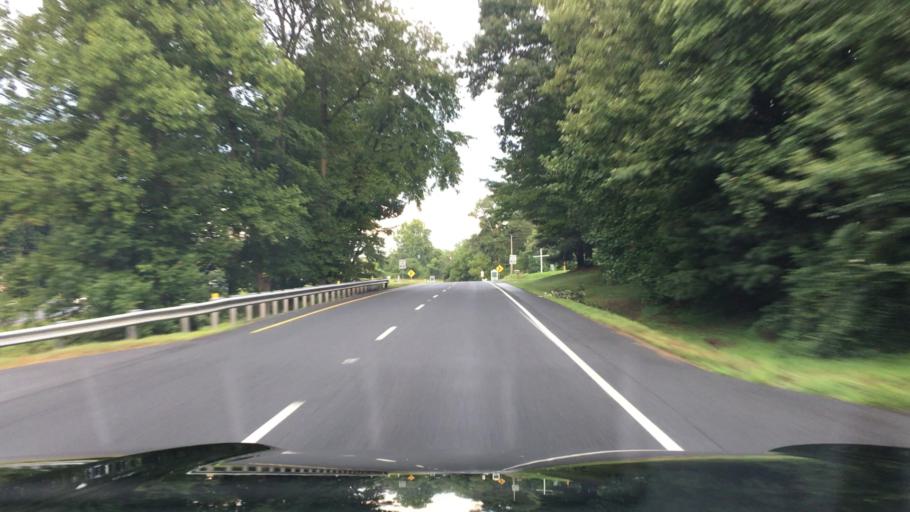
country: US
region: Virginia
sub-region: Culpeper County
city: Merrimac
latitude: 38.4497
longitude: -78.0937
